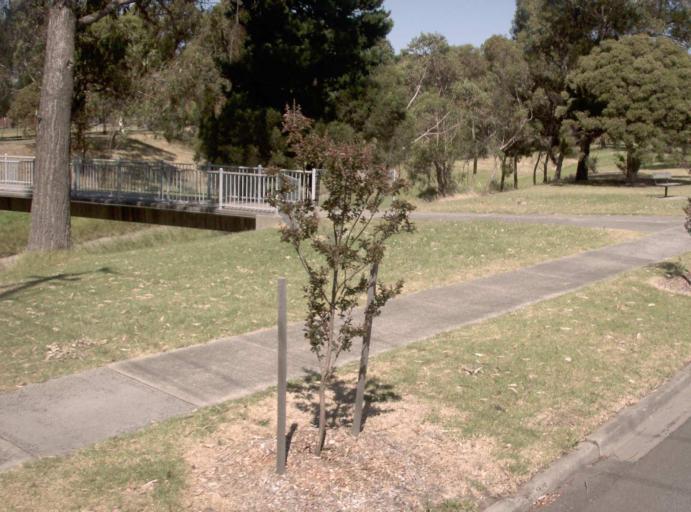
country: AU
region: Victoria
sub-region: Casey
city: Doveton
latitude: -37.9965
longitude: 145.2191
